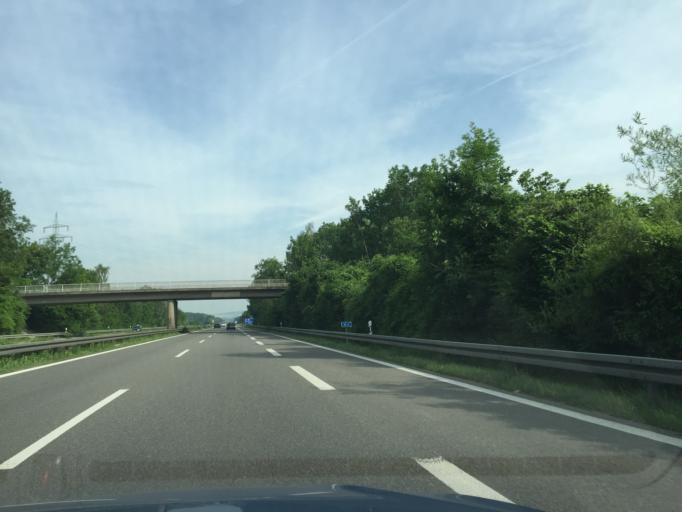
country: DE
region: Bavaria
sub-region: Swabia
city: Senden
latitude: 48.3519
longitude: 10.0143
